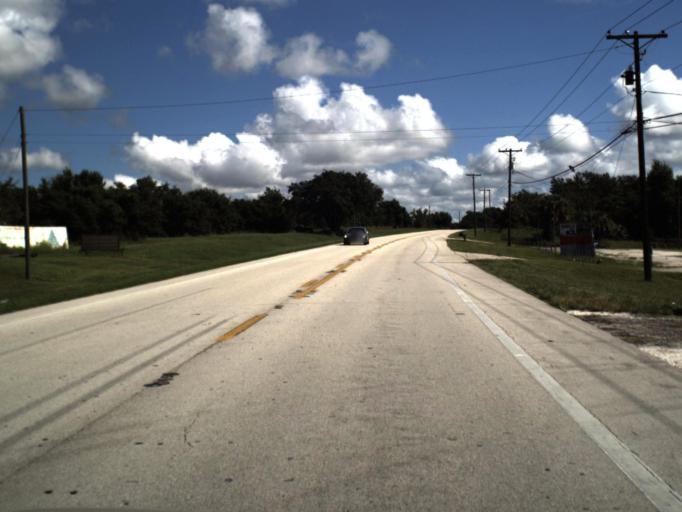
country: US
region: Florida
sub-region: Polk County
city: Davenport
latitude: 28.1494
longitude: -81.6103
